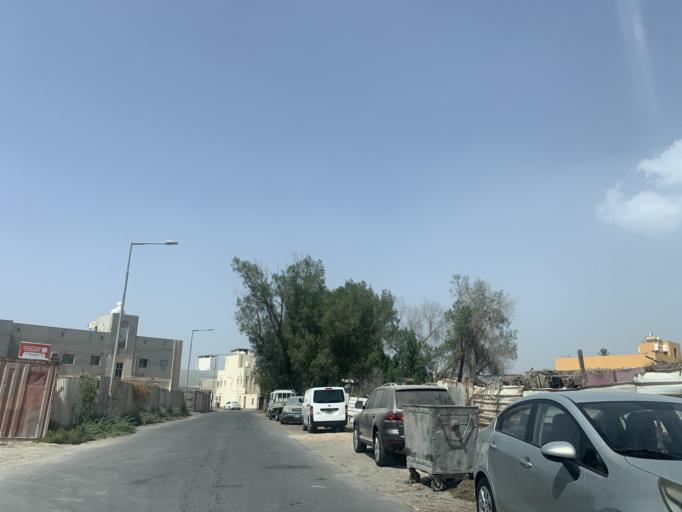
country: BH
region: Central Governorate
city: Madinat Hamad
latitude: 26.1485
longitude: 50.4954
